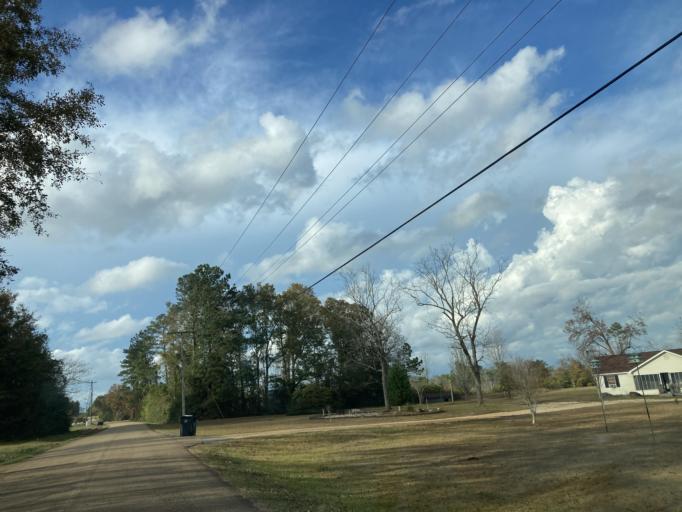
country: US
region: Mississippi
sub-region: Lamar County
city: Purvis
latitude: 31.1318
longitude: -89.6160
